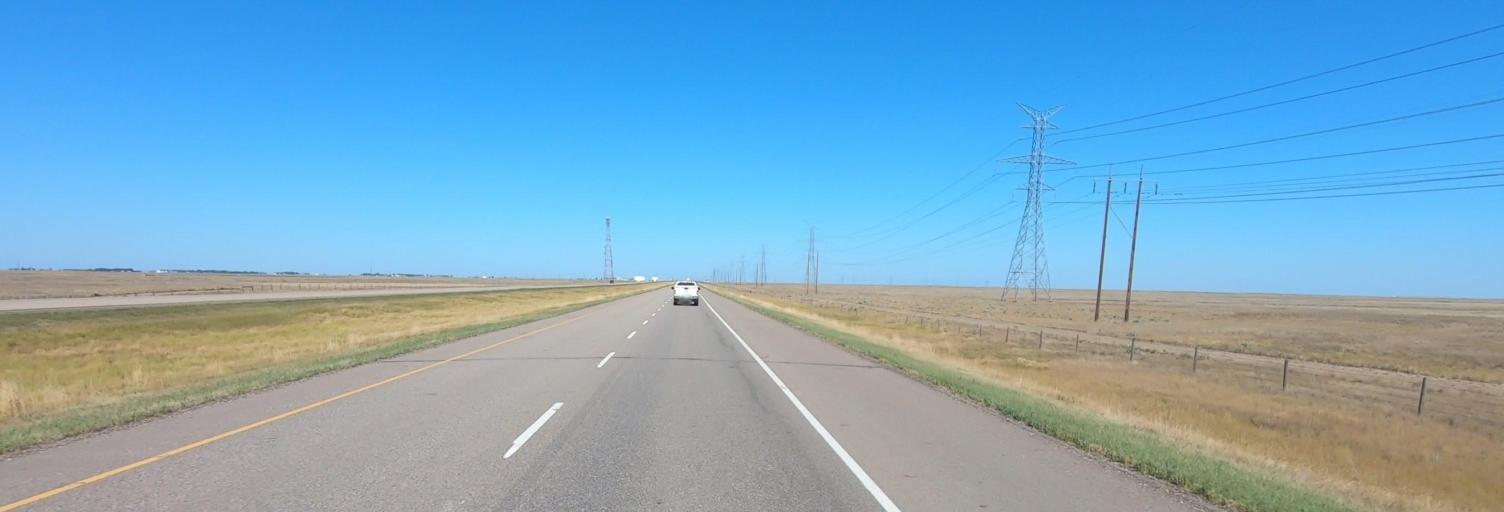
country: CA
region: Alberta
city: Brooks
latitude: 50.4380
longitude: -111.5524
